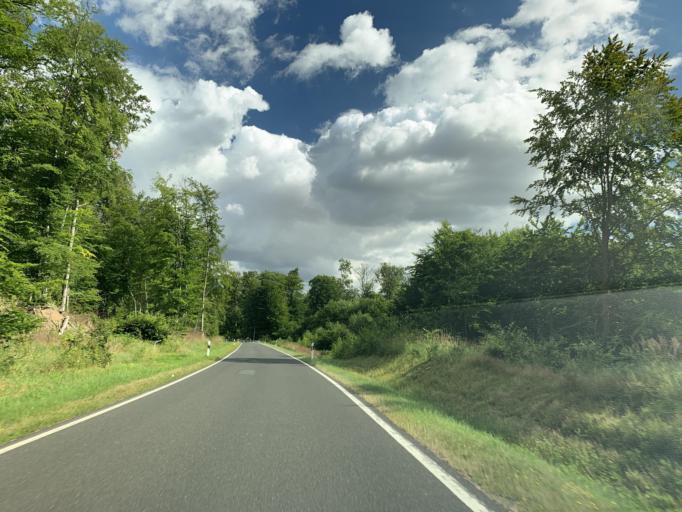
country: DE
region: Mecklenburg-Vorpommern
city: Wustrow
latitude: 53.4109
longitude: 13.1710
